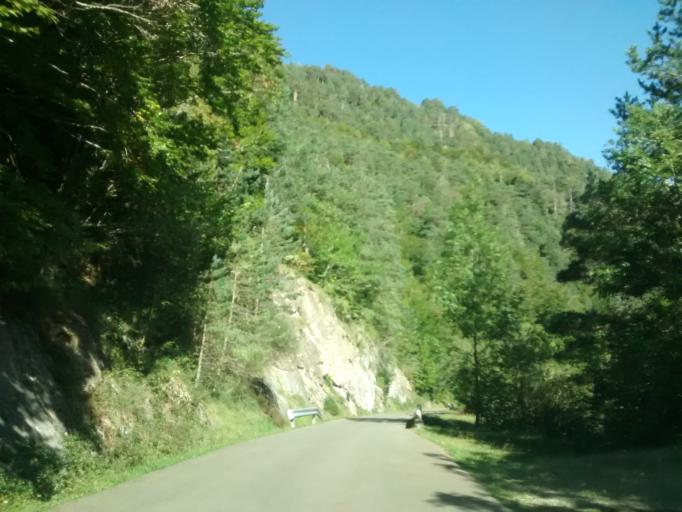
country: ES
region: Aragon
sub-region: Provincia de Huesca
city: Aragues del Puerto
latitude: 42.8140
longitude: -0.7129
